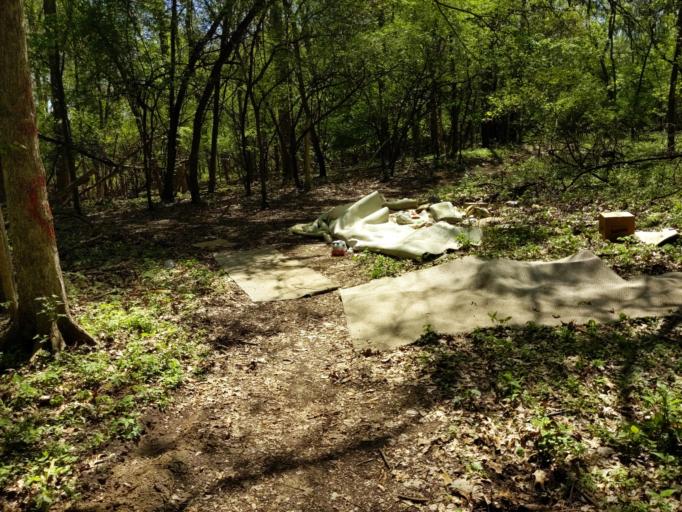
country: US
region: Michigan
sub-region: Kent County
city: Kentwood
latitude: 42.9098
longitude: -85.6503
